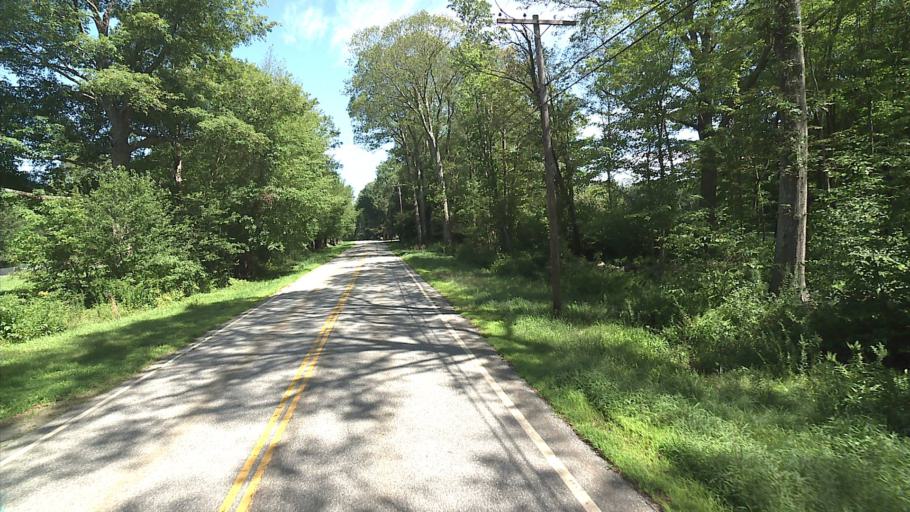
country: US
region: Connecticut
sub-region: Windham County
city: Windham
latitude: 41.7241
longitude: -72.0686
